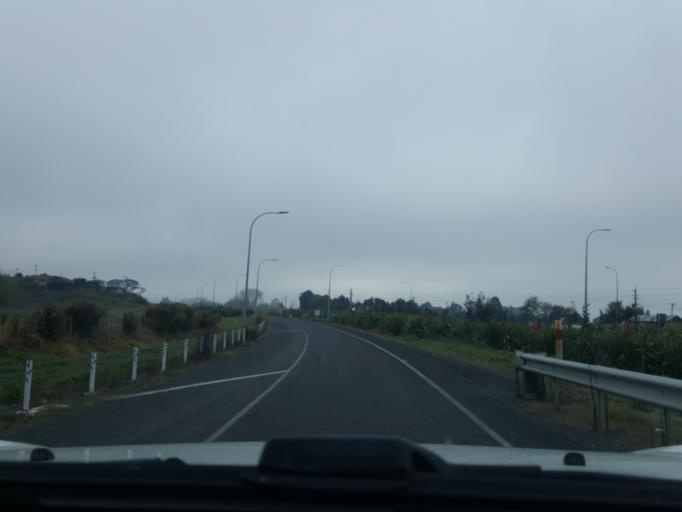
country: NZ
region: Waikato
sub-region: Waikato District
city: Te Kauwhata
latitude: -37.4119
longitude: 175.1248
